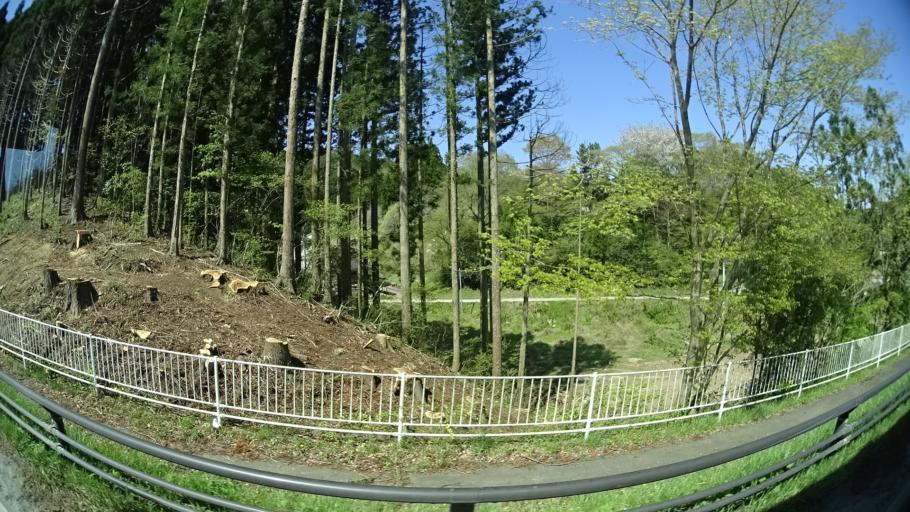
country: JP
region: Iwate
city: Ofunato
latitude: 38.9877
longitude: 141.6157
